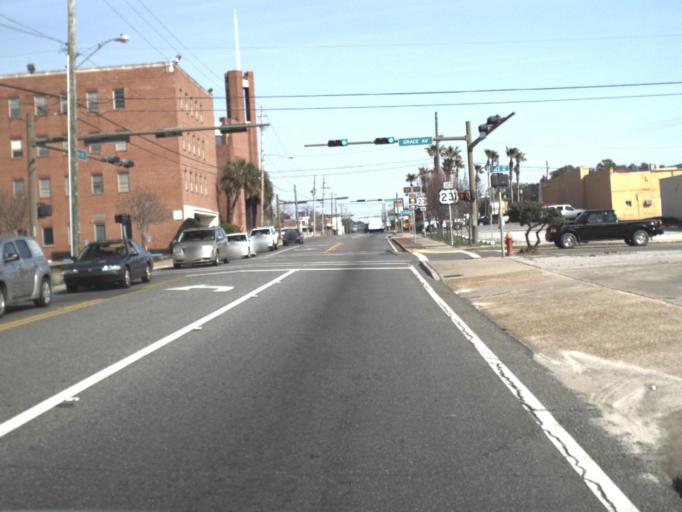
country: US
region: Florida
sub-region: Bay County
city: Panama City
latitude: 30.1588
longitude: -85.6619
